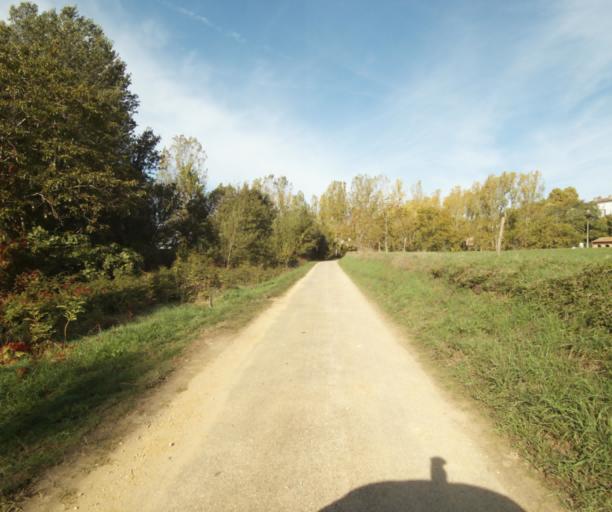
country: FR
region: Midi-Pyrenees
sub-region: Departement du Tarn-et-Garonne
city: Nohic
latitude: 43.9037
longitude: 1.4553
